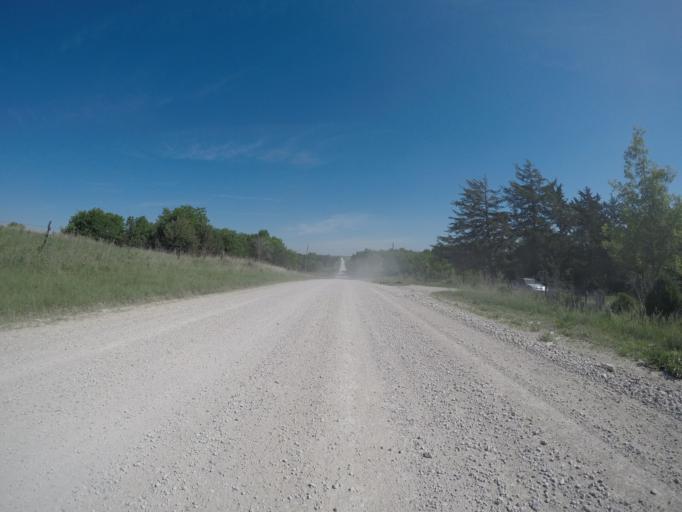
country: US
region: Kansas
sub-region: Wabaunsee County
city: Alma
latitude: 38.9899
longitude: -96.1138
